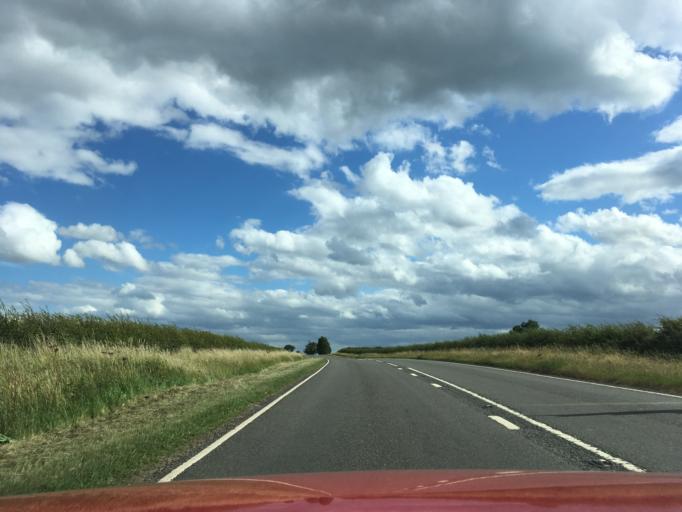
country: GB
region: England
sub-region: Warwickshire
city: Hartshill
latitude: 52.5961
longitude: -1.4787
